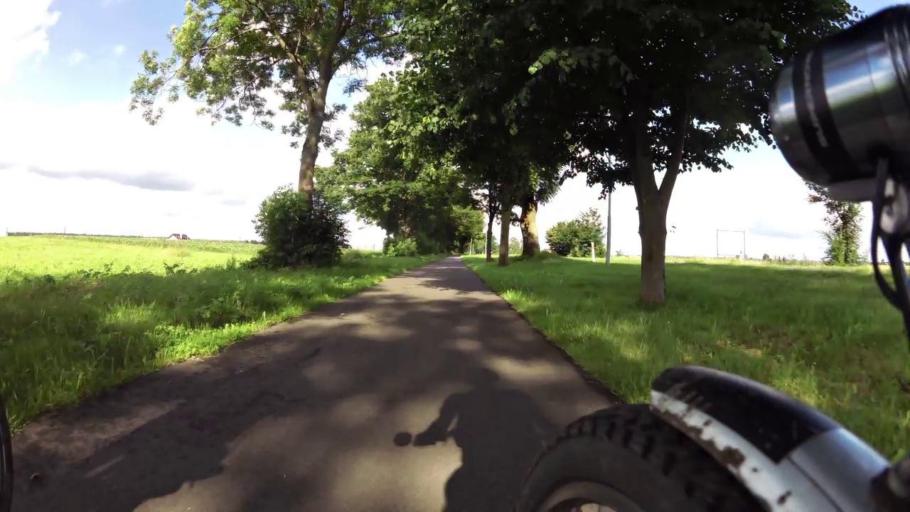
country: PL
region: West Pomeranian Voivodeship
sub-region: Powiat swidwinski
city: Swidwin
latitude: 53.7763
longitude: 15.8104
